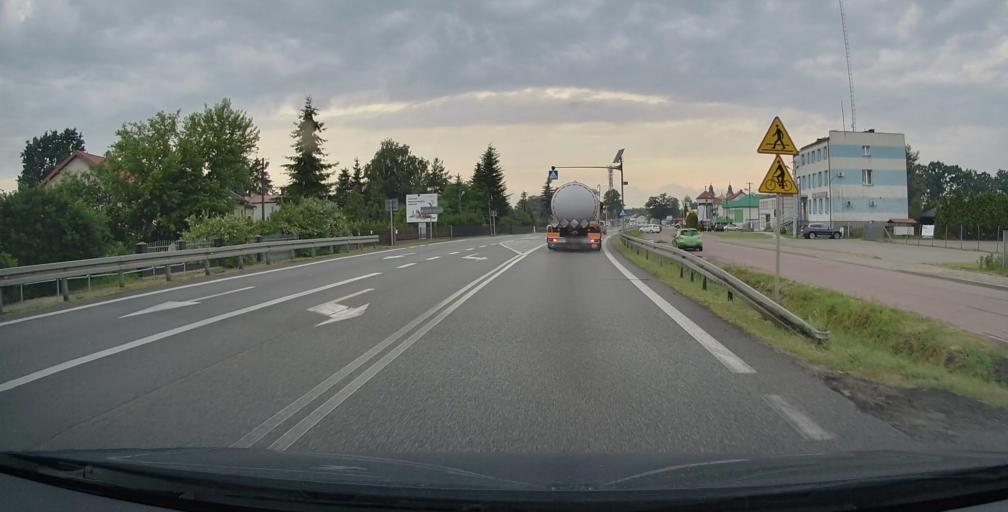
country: PL
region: Masovian Voivodeship
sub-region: Powiat siedlecki
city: Zbuczyn
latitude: 52.0876
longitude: 22.4441
